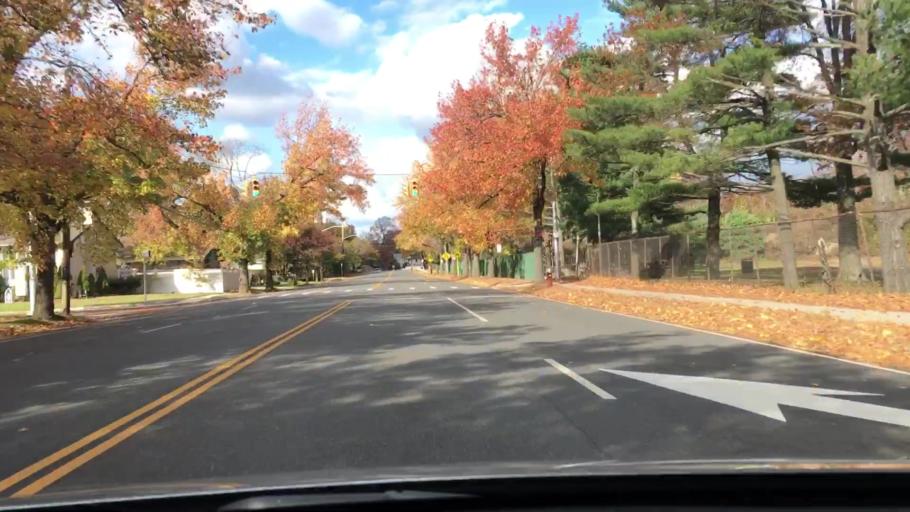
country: US
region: New York
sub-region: Nassau County
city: New Cassel
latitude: 40.7718
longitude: -73.5510
